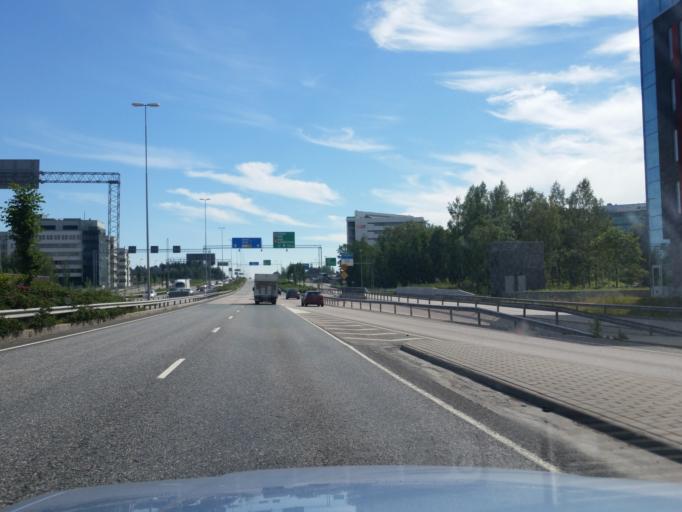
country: FI
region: Uusimaa
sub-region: Helsinki
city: Teekkarikylae
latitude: 60.2151
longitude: 24.8159
